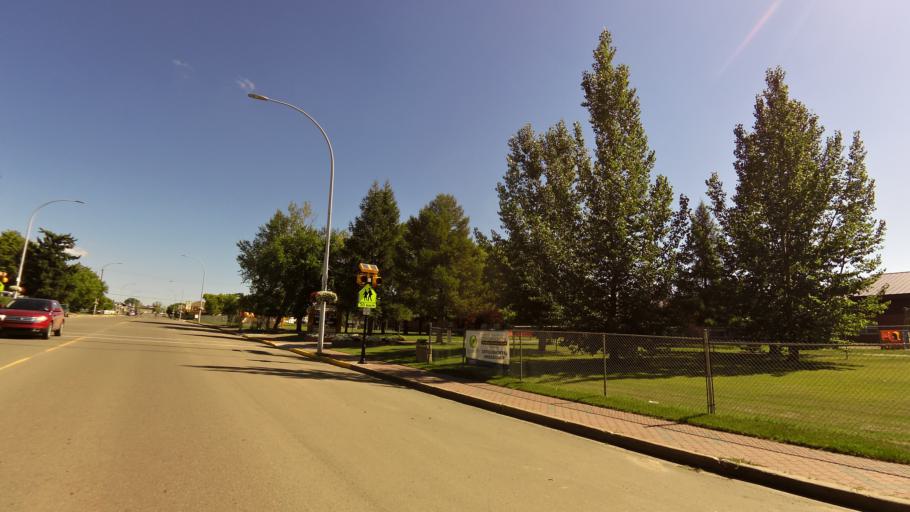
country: CA
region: Alberta
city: Wainwright
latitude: 52.8390
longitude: -110.8549
